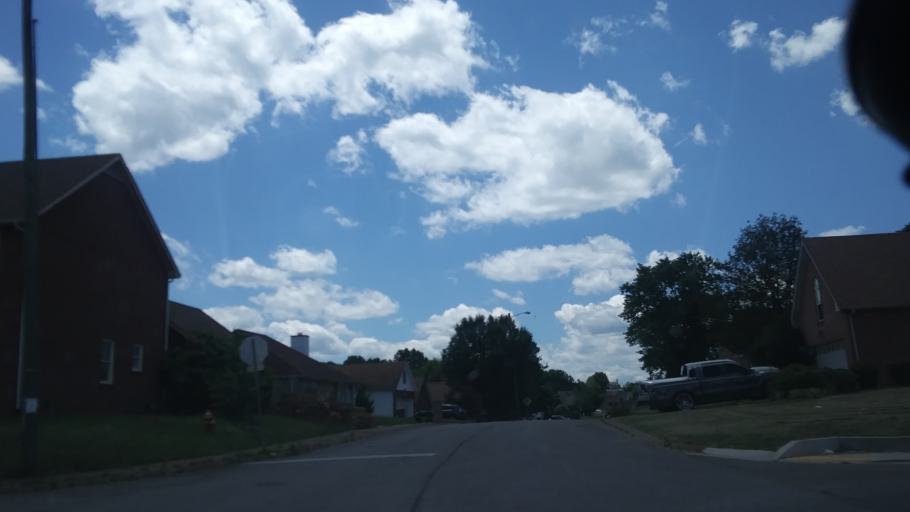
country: US
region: Tennessee
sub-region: Rutherford County
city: La Vergne
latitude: 36.0880
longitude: -86.6530
